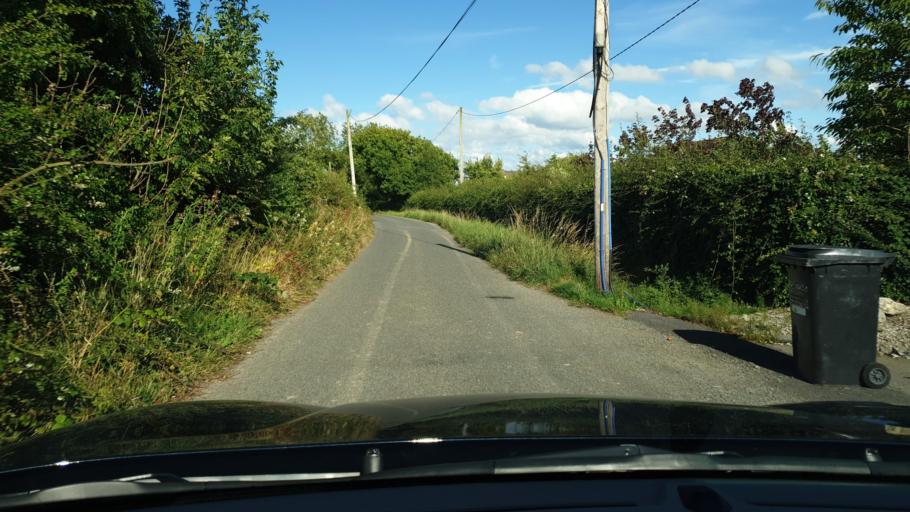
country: IE
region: Leinster
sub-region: An Mhi
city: Ashbourne
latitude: 53.5258
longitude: -6.3730
